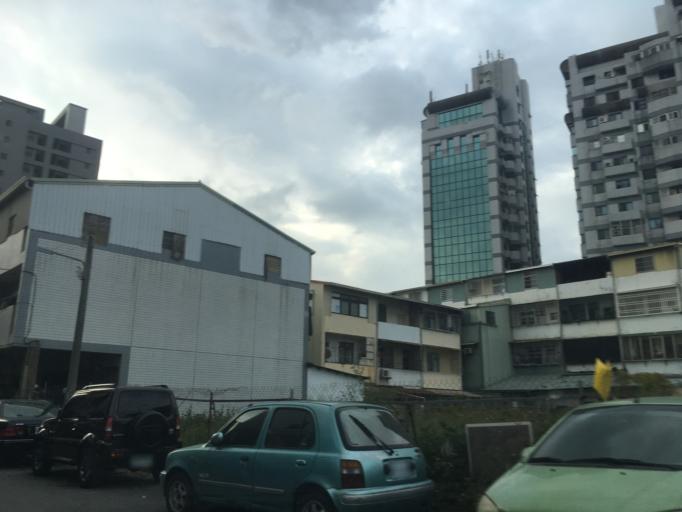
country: TW
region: Taiwan
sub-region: Taichung City
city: Taichung
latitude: 24.1690
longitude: 120.7085
